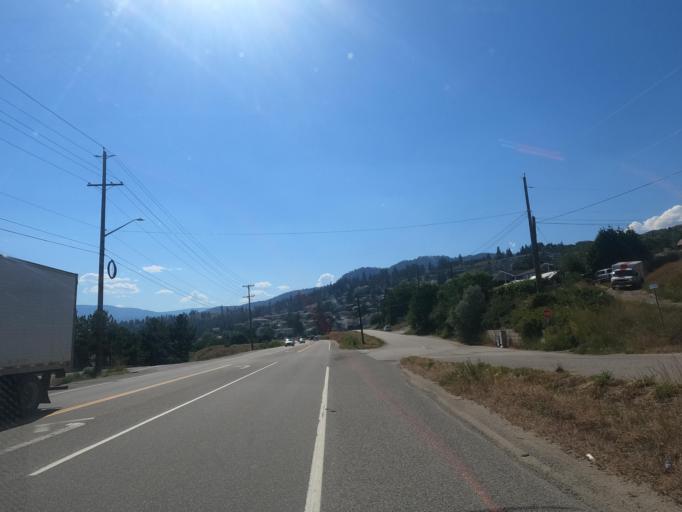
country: CA
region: British Columbia
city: Peachland
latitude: 49.7957
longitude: -119.6974
